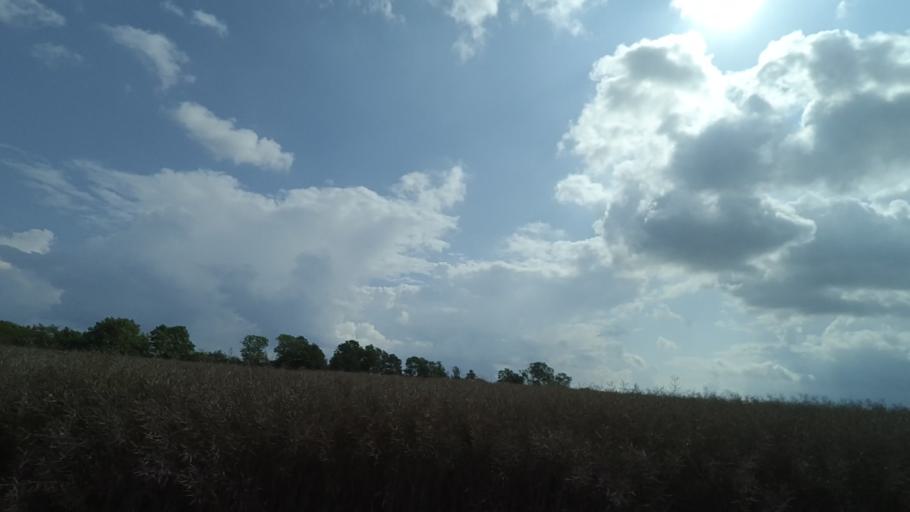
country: DK
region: Central Jutland
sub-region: Norddjurs Kommune
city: Allingabro
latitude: 56.5445
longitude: 10.3635
